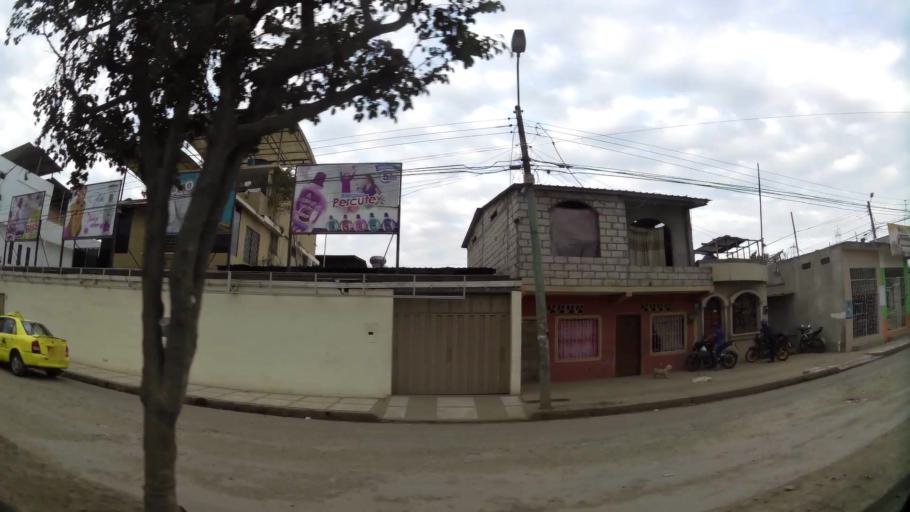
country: EC
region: El Oro
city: Machala
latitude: -3.2692
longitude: -79.9382
